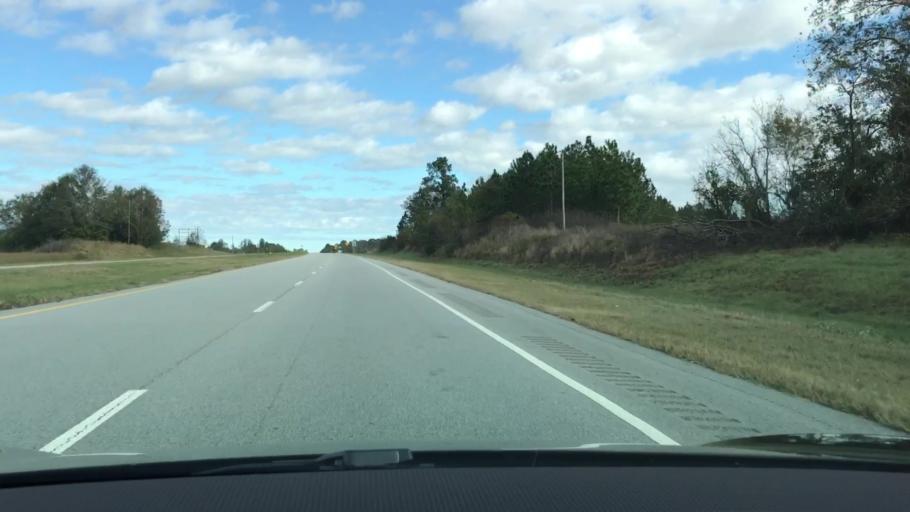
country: US
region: Georgia
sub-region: Jefferson County
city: Wadley
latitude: 32.8393
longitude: -82.3994
